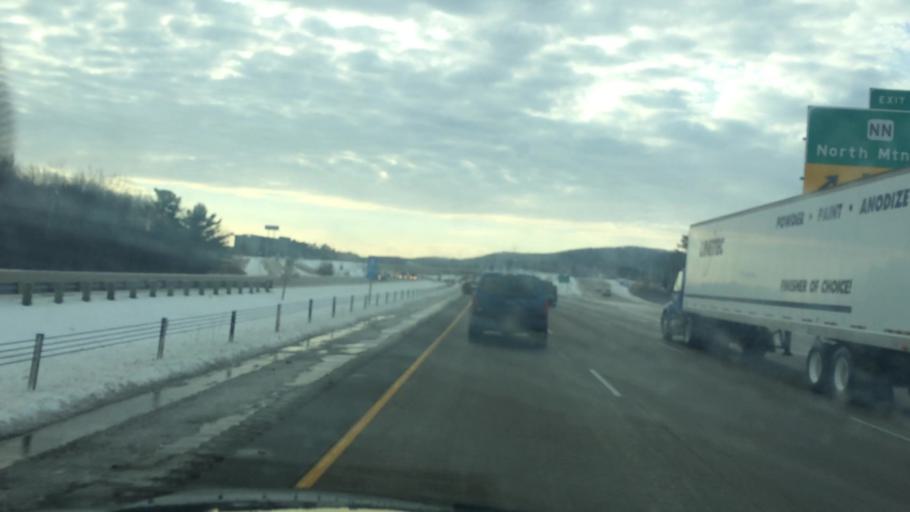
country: US
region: Wisconsin
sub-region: Marathon County
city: Rib Mountain
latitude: 44.9371
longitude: -89.6659
